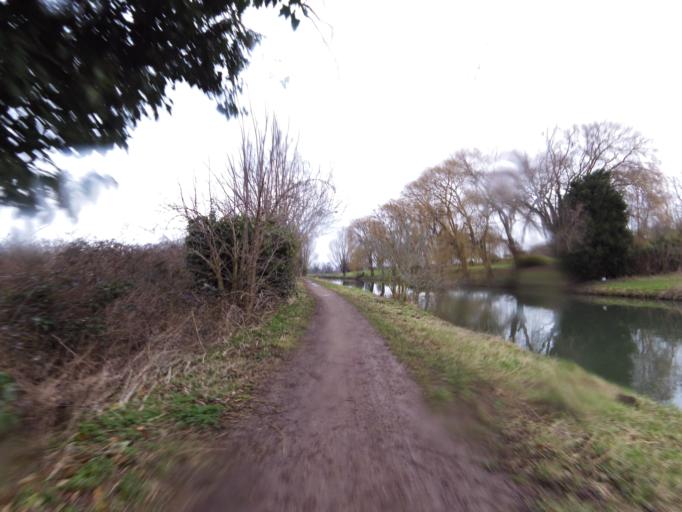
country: GB
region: England
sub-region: Cambridgeshire
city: Waterbeach
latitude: 52.2429
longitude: 0.1837
